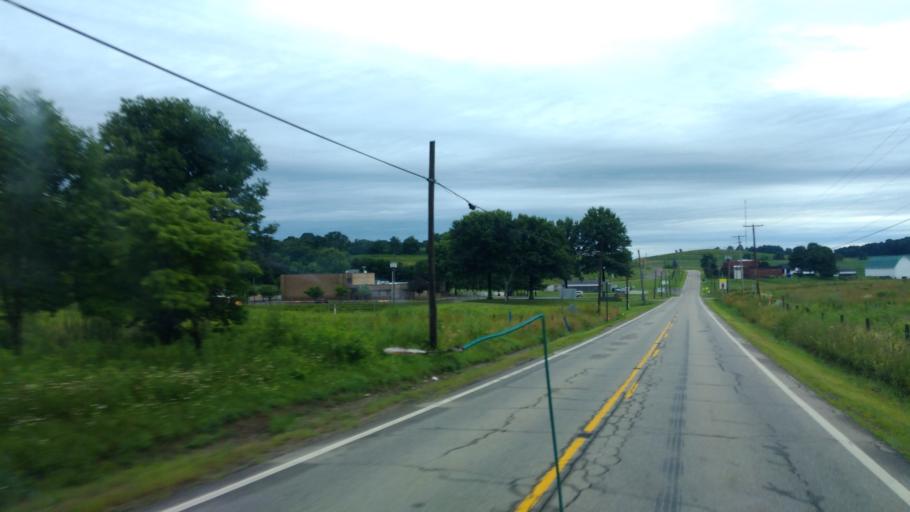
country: US
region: Ohio
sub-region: Carroll County
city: Carrollton
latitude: 40.6102
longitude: -81.0682
